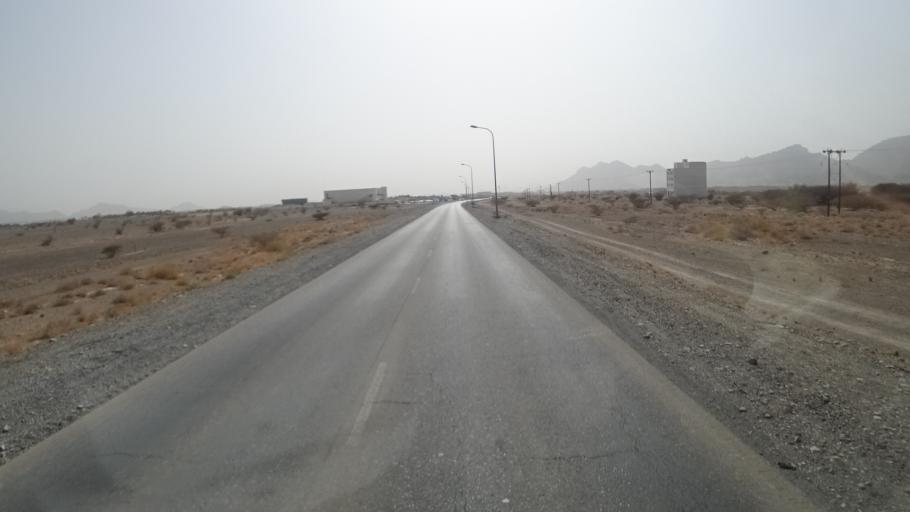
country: OM
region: Muhafazat ad Dakhiliyah
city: Nizwa
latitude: 22.9184
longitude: 57.6123
